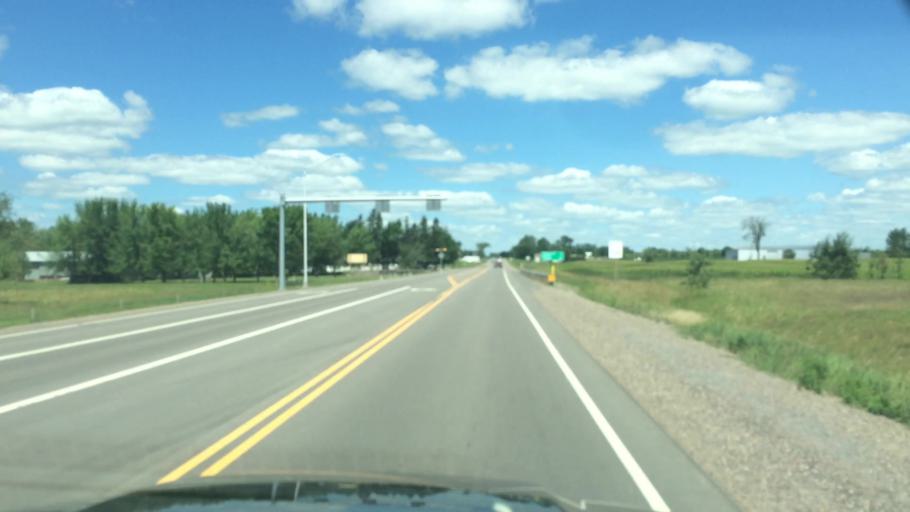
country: US
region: Wisconsin
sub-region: Clark County
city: Abbotsford
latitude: 45.0044
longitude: -90.3157
